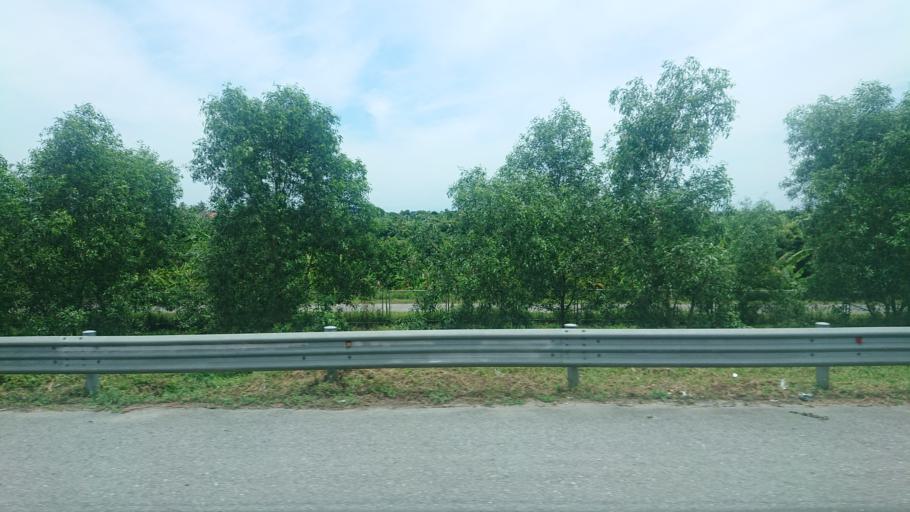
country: VN
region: Hai Phong
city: An Lao
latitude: 20.8101
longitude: 106.5069
